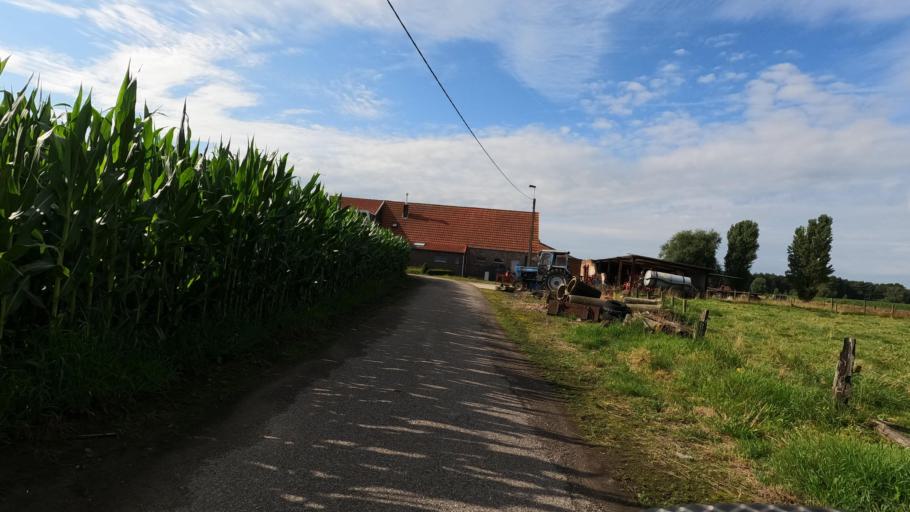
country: BE
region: Flanders
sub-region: Provincie Antwerpen
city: Rumst
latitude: 51.0938
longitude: 4.4282
